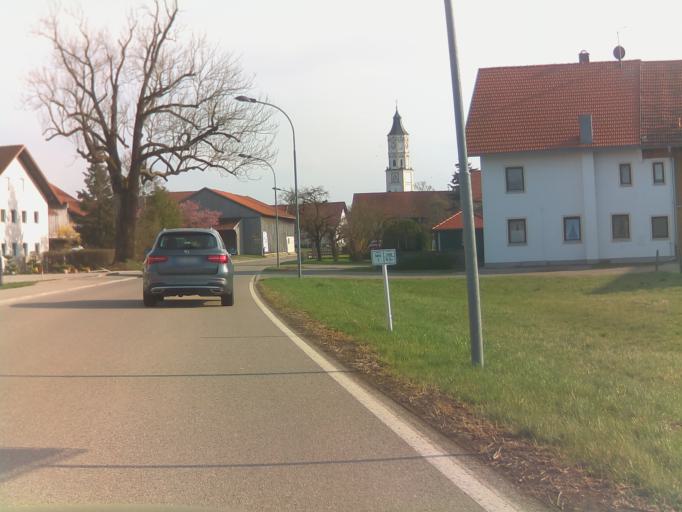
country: DE
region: Bavaria
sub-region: Swabia
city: Rieden
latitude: 47.9731
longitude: 10.6213
